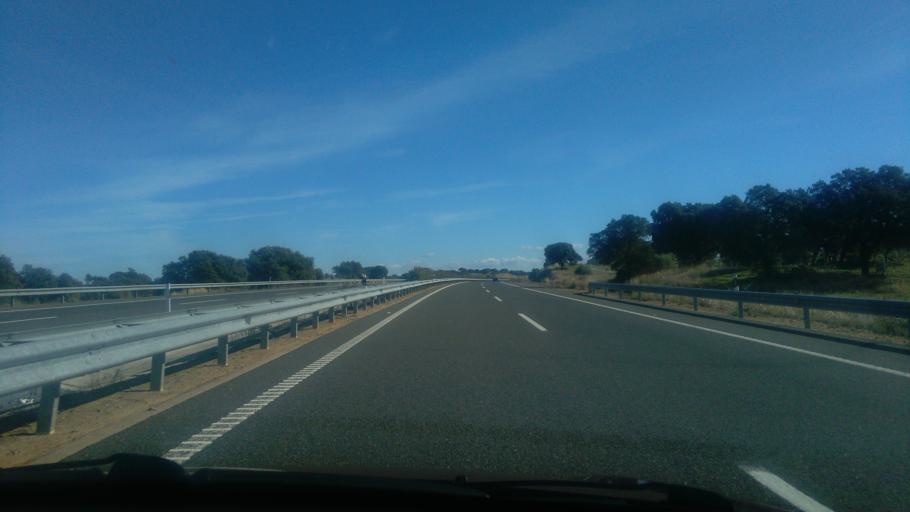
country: ES
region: Extremadura
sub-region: Provincia de Caceres
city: Plasenzuela
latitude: 39.4427
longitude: -6.0418
